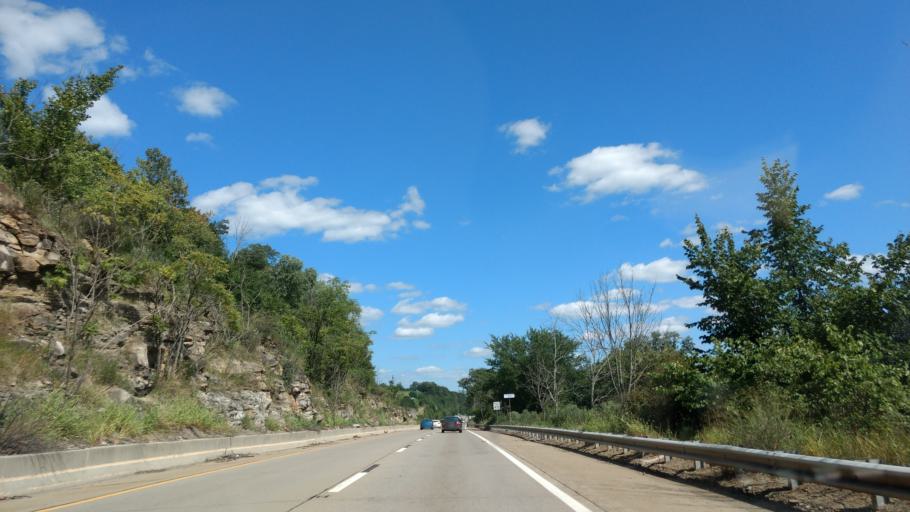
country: US
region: Pennsylvania
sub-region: Allegheny County
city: Emsworth
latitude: 40.5159
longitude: -80.1219
